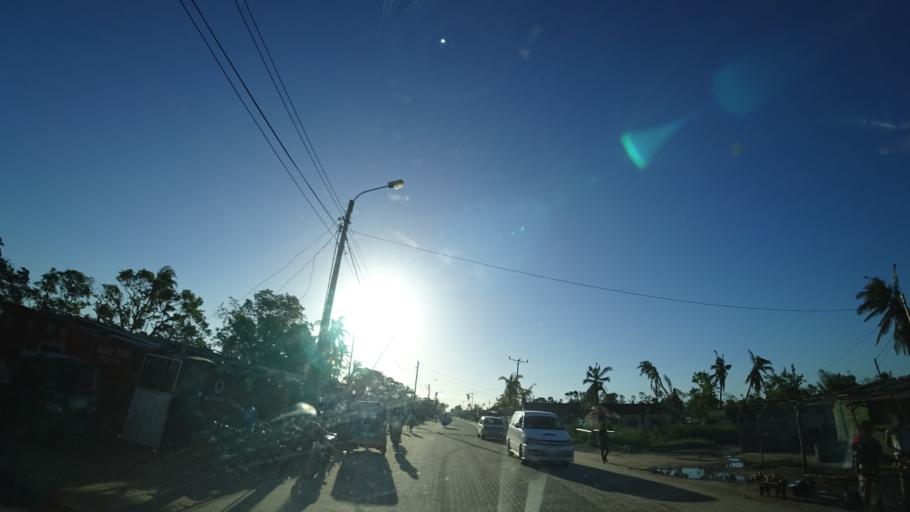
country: MZ
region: Sofala
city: Beira
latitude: -19.7493
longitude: 34.8528
